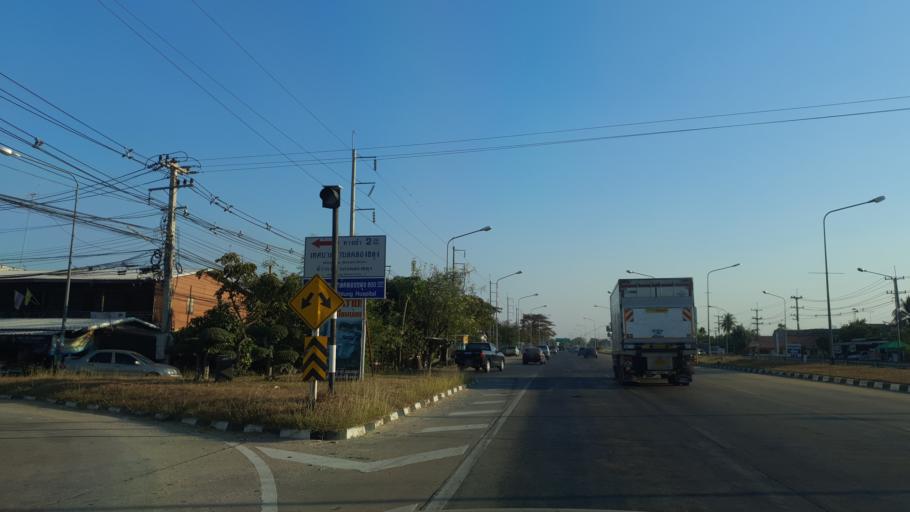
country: TH
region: Kamphaeng Phet
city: Khlong Khlung
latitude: 16.2134
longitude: 99.7030
